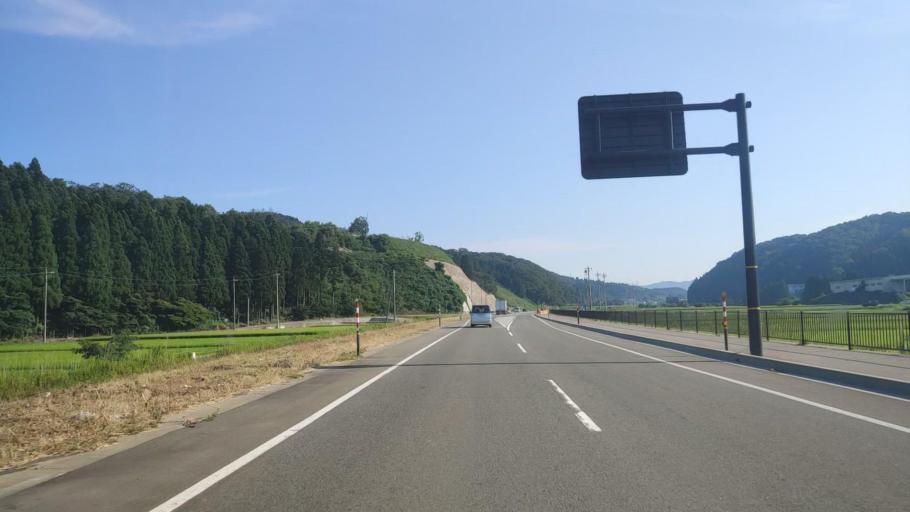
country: JP
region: Fukui
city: Maruoka
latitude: 36.2051
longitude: 136.2678
